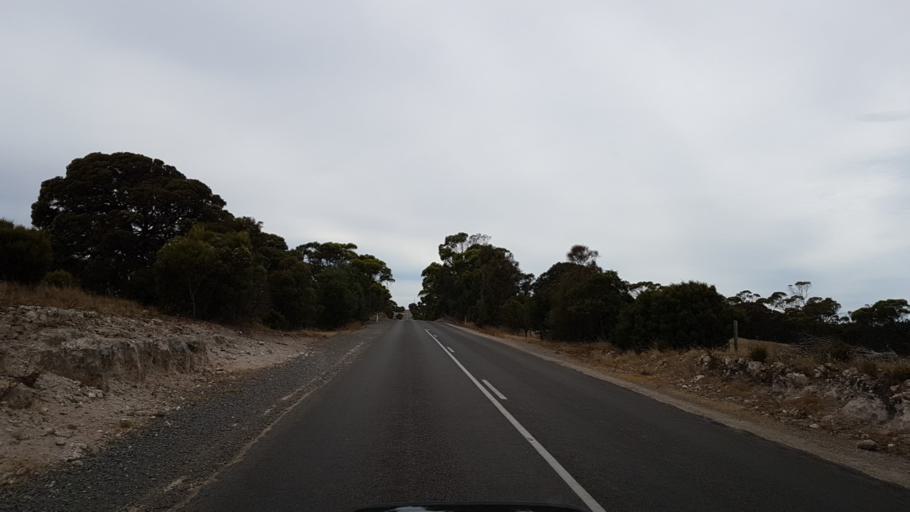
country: AU
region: South Australia
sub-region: Yorke Peninsula
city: Honiton
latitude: -34.9850
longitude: 137.2402
